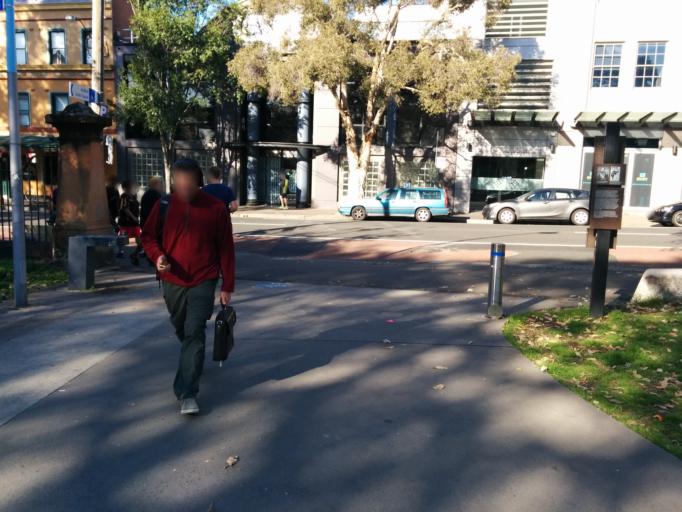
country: AU
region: New South Wales
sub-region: City of Sydney
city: Redfern
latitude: -33.8870
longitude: 151.2054
